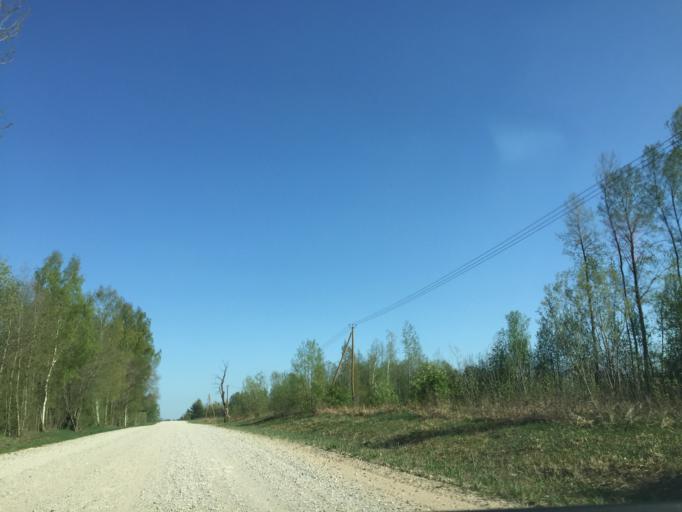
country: LV
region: Skriveri
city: Skriveri
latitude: 56.8377
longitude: 25.1113
